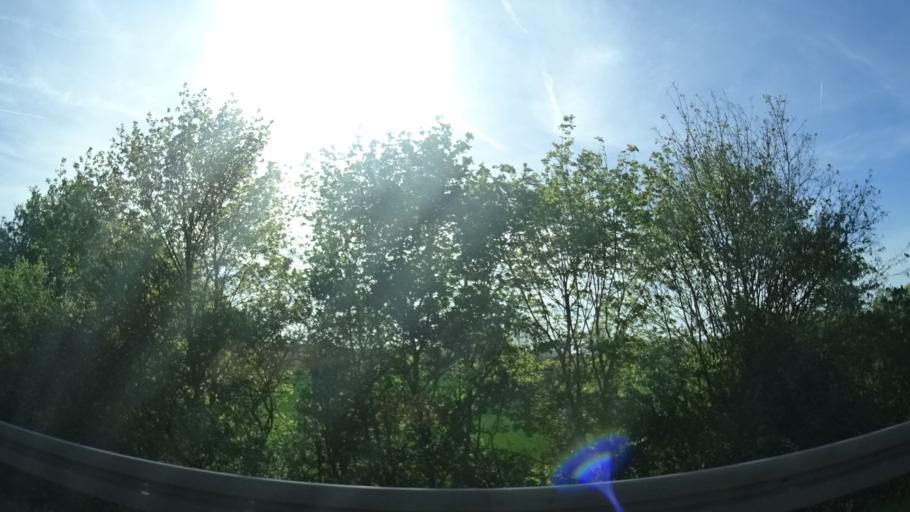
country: DE
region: Bavaria
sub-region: Regierungsbezirk Unterfranken
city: Wonfurt
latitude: 50.0089
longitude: 10.4344
